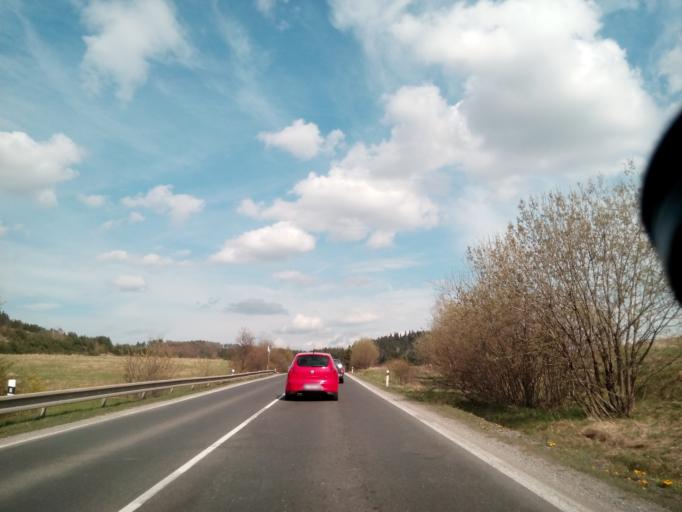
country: SK
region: Presovsky
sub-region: Okres Presov
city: Levoca
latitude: 49.0310
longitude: 20.6078
